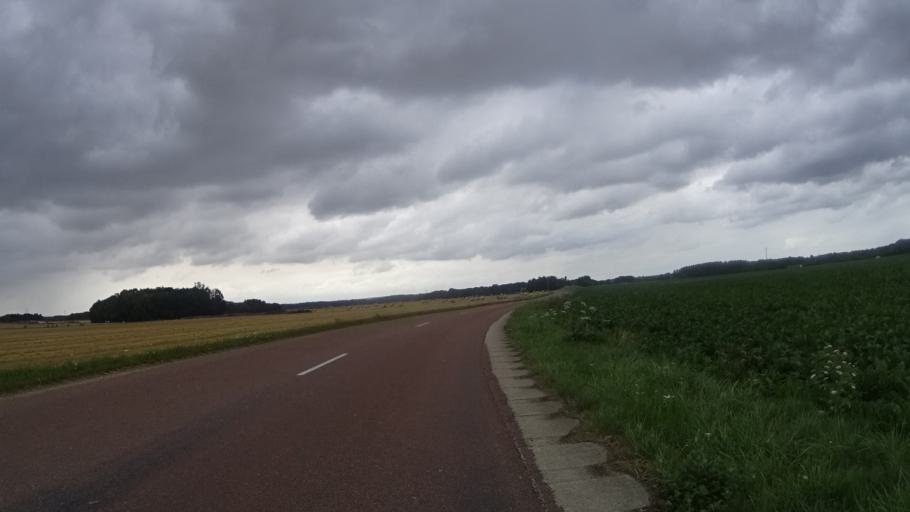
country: FR
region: Champagne-Ardenne
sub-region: Departement de l'Aube
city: Verrieres
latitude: 48.2373
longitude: 4.1649
